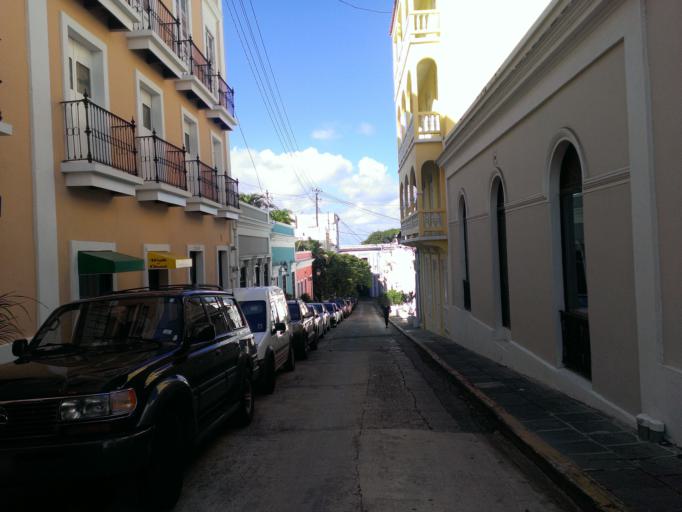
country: PR
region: San Juan
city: San Juan
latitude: 18.4651
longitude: -66.1181
